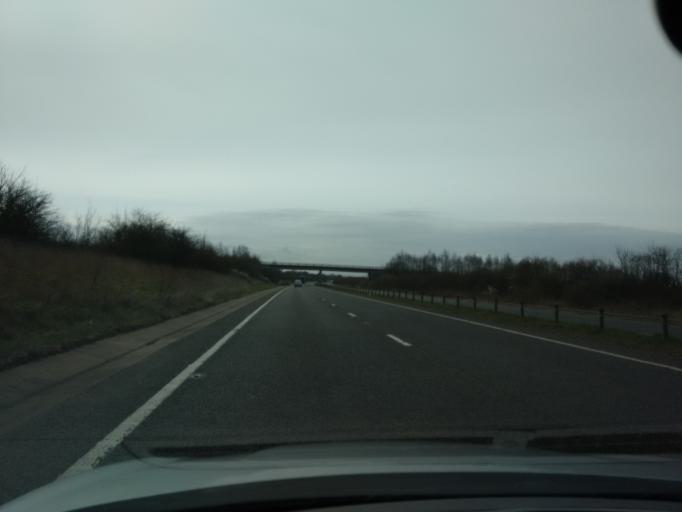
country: GB
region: England
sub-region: Warwickshire
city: Bidford-on-avon
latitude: 52.1800
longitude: -1.8790
